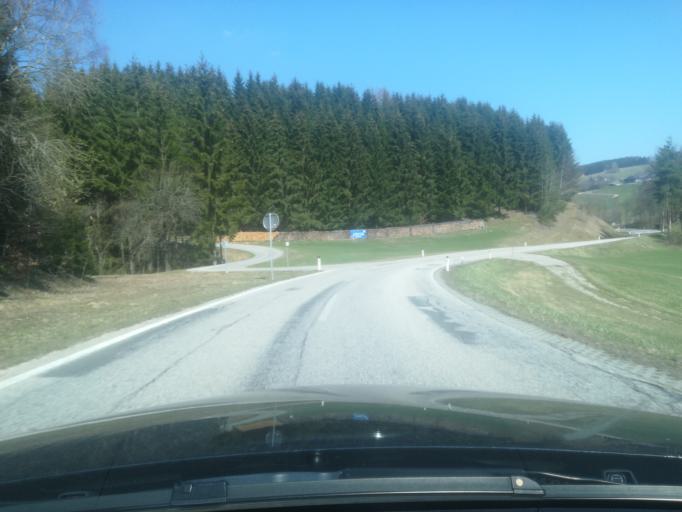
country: AT
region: Upper Austria
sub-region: Politischer Bezirk Perg
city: Sankt Georgen am Walde
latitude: 48.4244
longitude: 14.7719
